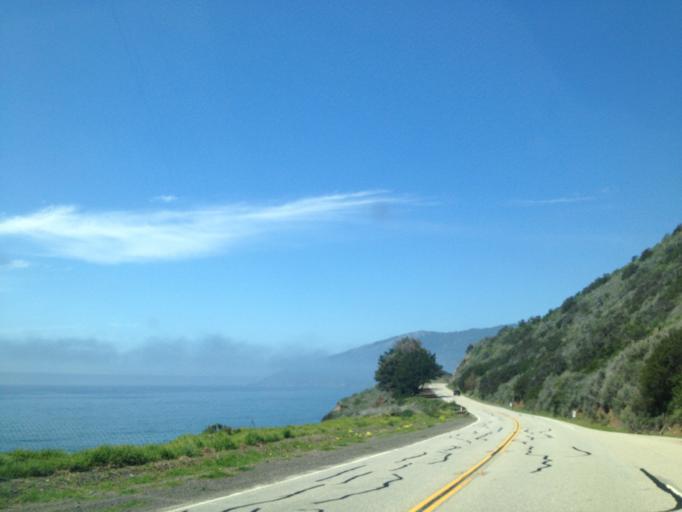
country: US
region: California
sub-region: Monterey County
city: Greenfield
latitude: 35.9704
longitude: -121.4845
